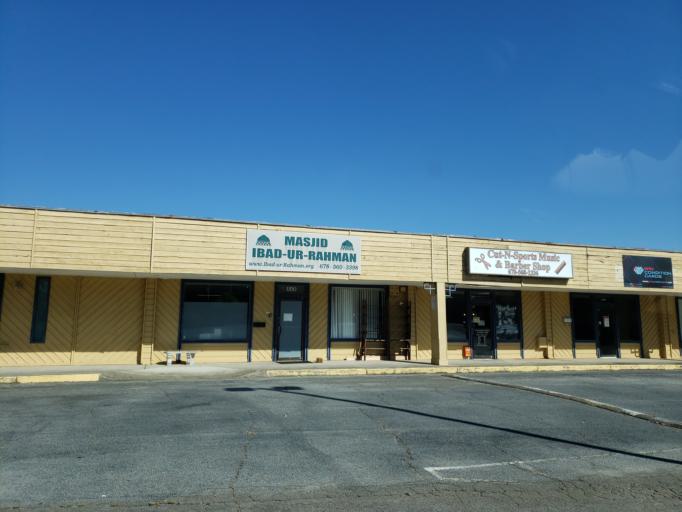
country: US
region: Georgia
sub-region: Cobb County
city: Marietta
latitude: 34.0140
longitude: -84.4933
